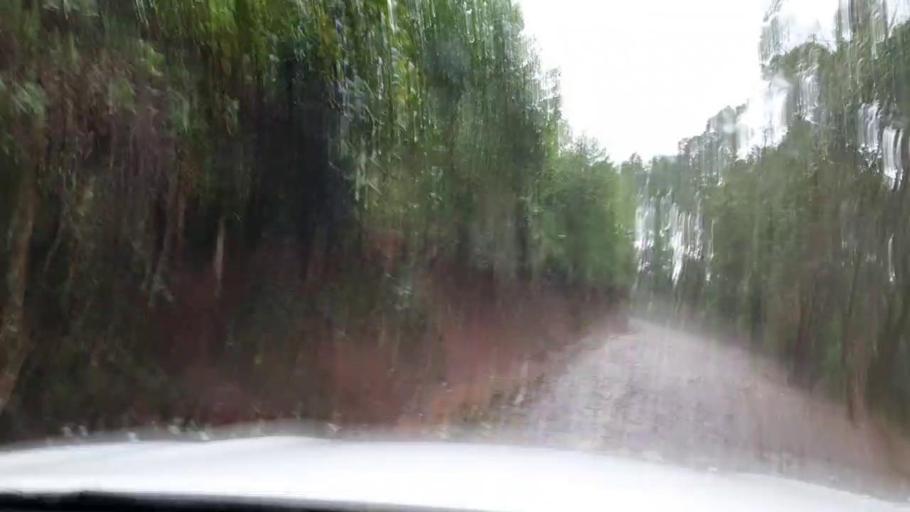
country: RW
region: Western Province
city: Cyangugu
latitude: -2.4672
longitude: 29.0345
